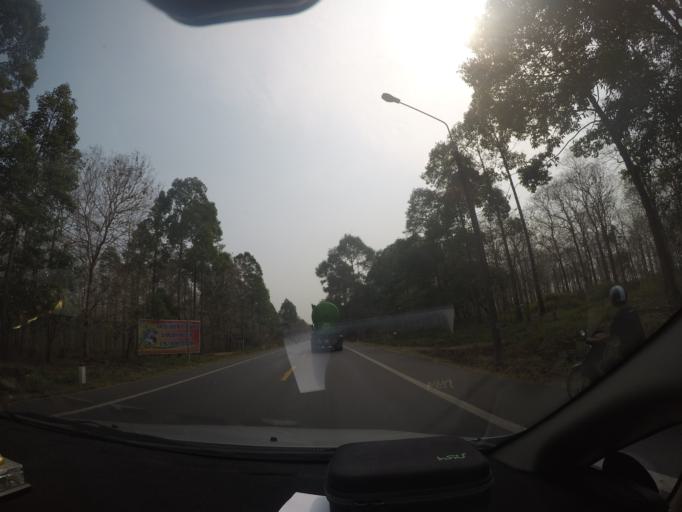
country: VN
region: Dong Nai
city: Tan Phu
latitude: 11.2477
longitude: 107.4014
